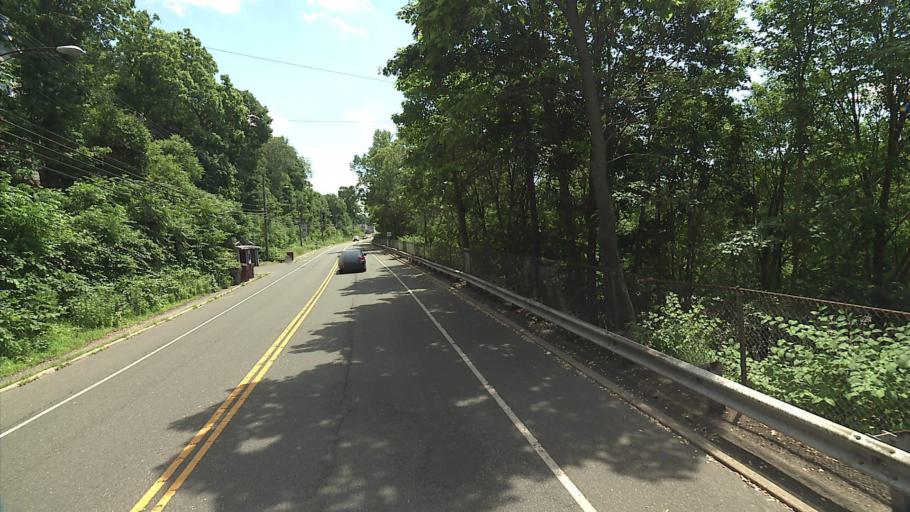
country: US
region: Connecticut
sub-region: New Haven County
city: Naugatuck
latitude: 41.4840
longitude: -73.0497
